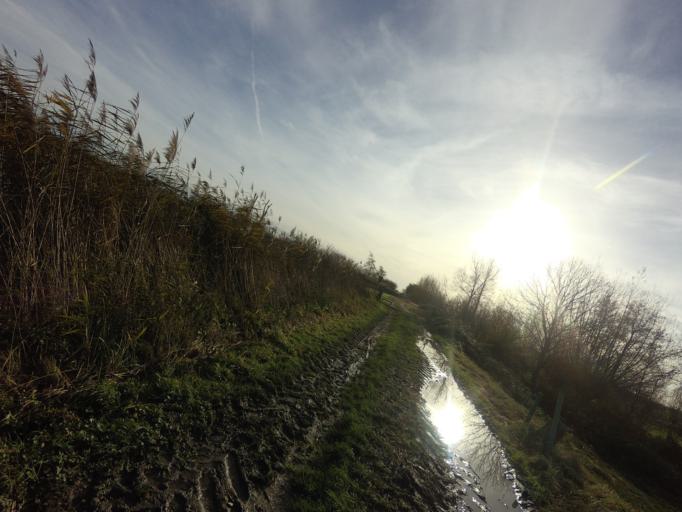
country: NL
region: South Holland
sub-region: Gemeente Vlist
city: Haastrecht
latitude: 52.0421
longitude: 4.7819
